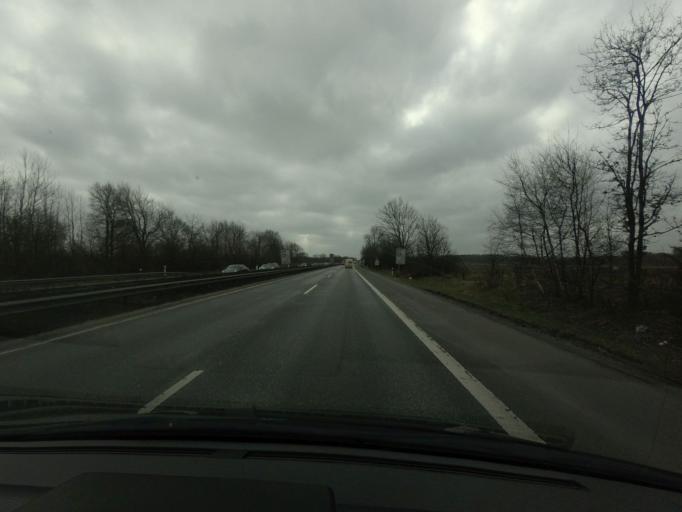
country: DE
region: Schleswig-Holstein
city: Bonningstedt
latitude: 53.6843
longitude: 9.9453
